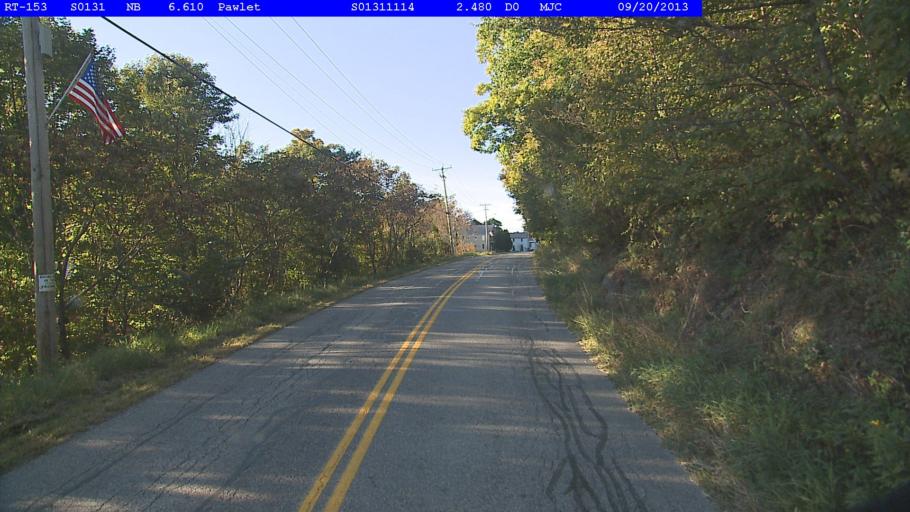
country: US
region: New York
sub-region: Washington County
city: Granville
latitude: 43.3487
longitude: -73.2490
